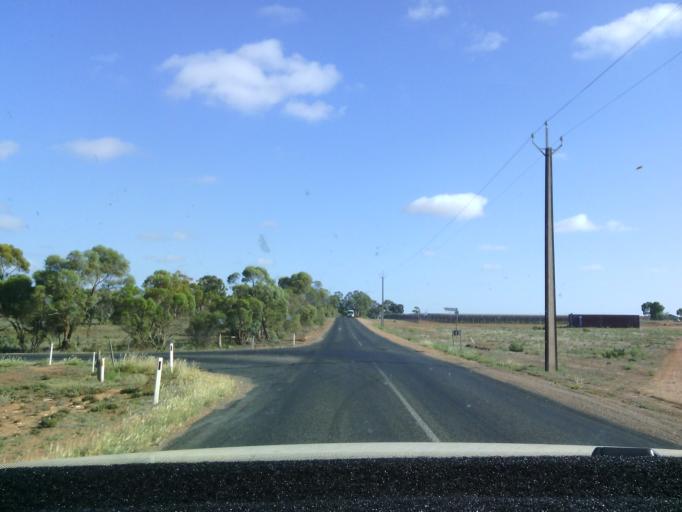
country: AU
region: South Australia
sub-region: Berri and Barmera
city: Monash
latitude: -34.2569
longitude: 140.5411
